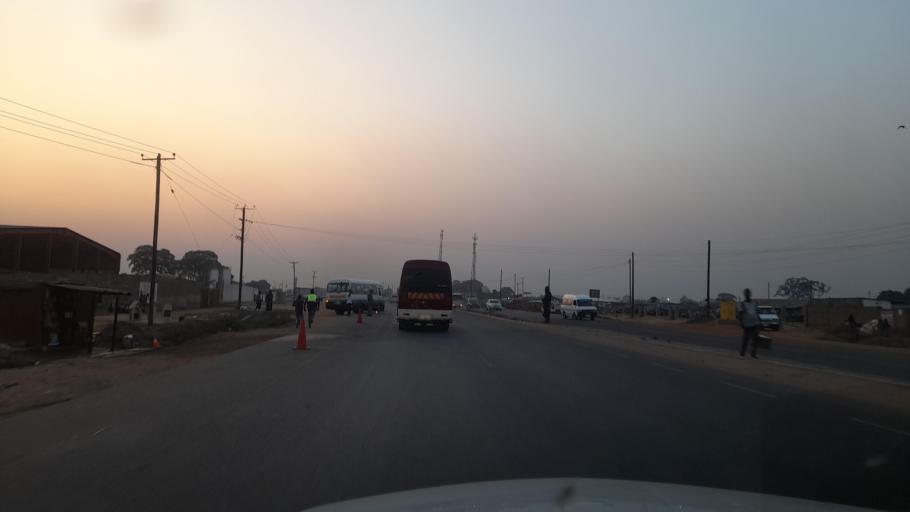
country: ZM
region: Copperbelt
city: Kitwe
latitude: -12.7765
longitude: 28.1926
